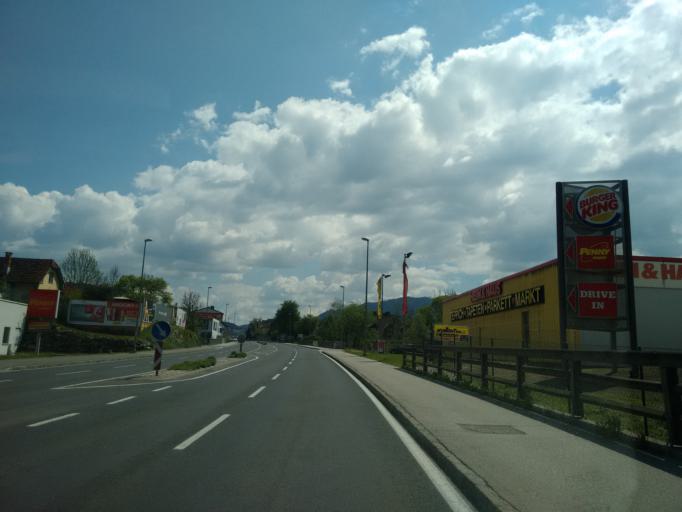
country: AT
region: Styria
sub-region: Politischer Bezirk Bruck-Muerzzuschlag
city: Bruck an der Mur
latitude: 47.4286
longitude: 15.2682
